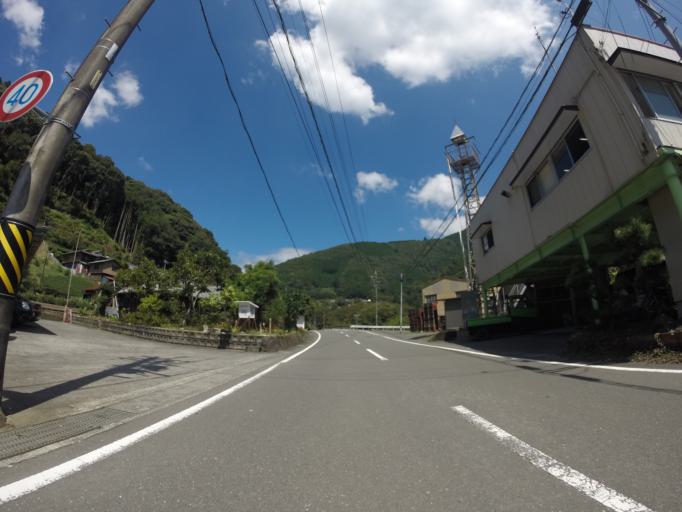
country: JP
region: Shizuoka
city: Shizuoka-shi
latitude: 35.0704
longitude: 138.2460
